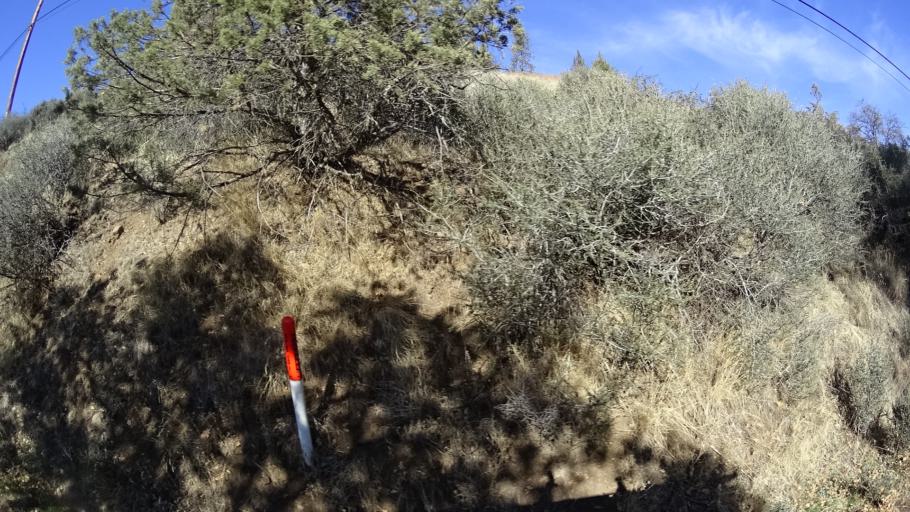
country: US
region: California
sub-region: Siskiyou County
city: Yreka
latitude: 41.7186
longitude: -122.6782
